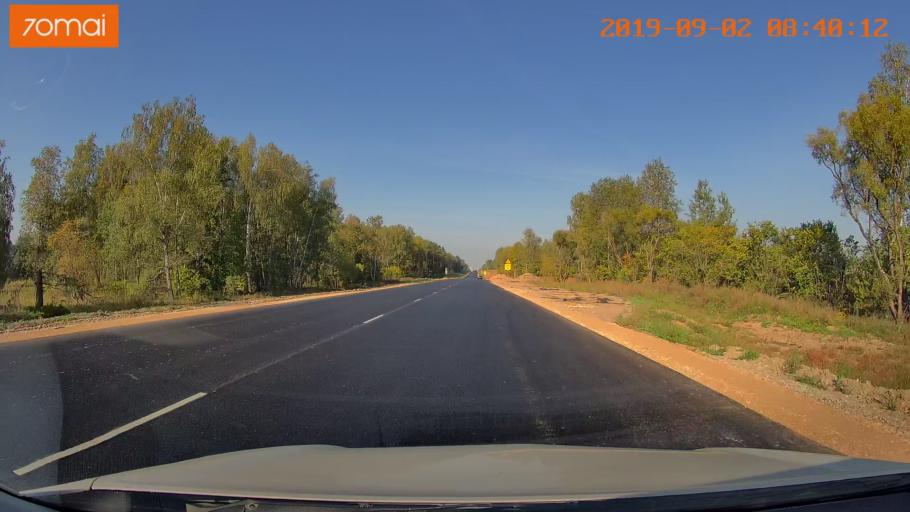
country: RU
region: Kaluga
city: Kudinovo
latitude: 54.9743
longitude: 36.1412
